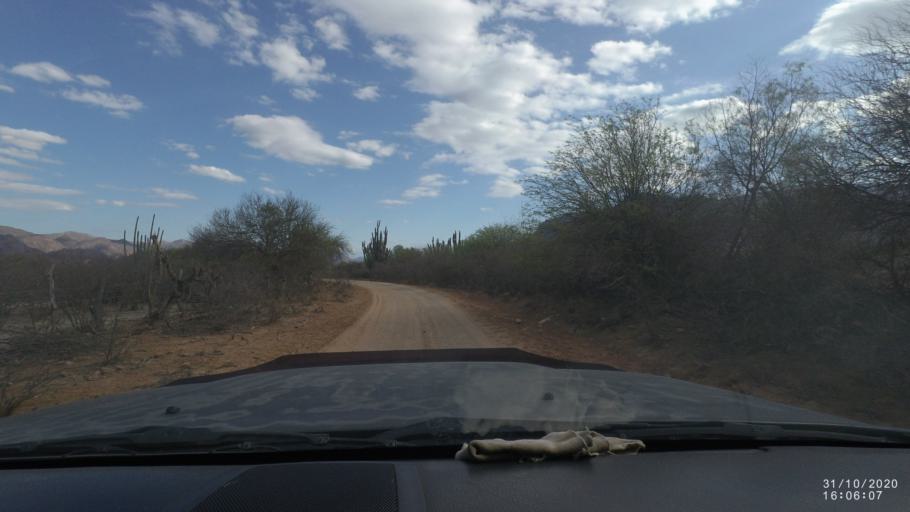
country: BO
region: Chuquisaca
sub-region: Provincia Zudanez
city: Mojocoya
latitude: -18.3712
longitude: -64.6486
